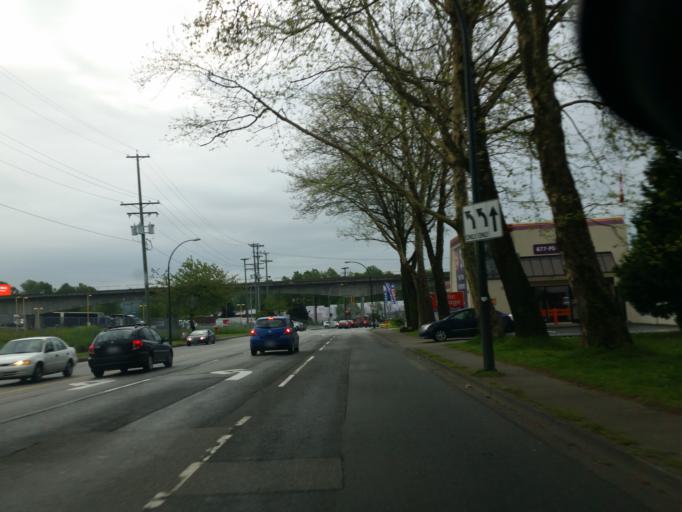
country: CA
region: British Columbia
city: New Westminster
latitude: 49.2315
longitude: -122.8851
